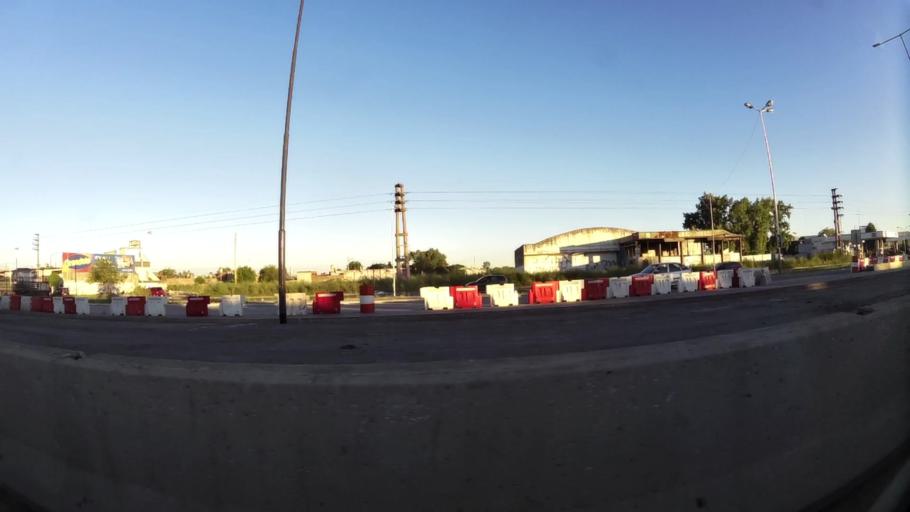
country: AR
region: Buenos Aires
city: Pontevedra
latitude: -34.7524
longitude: -58.6138
